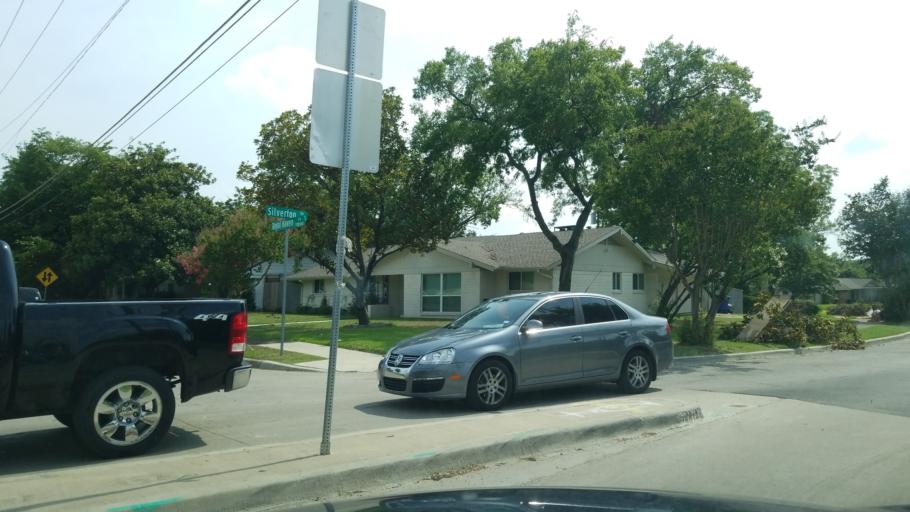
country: US
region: Texas
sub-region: Dallas County
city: Farmers Branch
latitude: 32.8997
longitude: -96.8724
